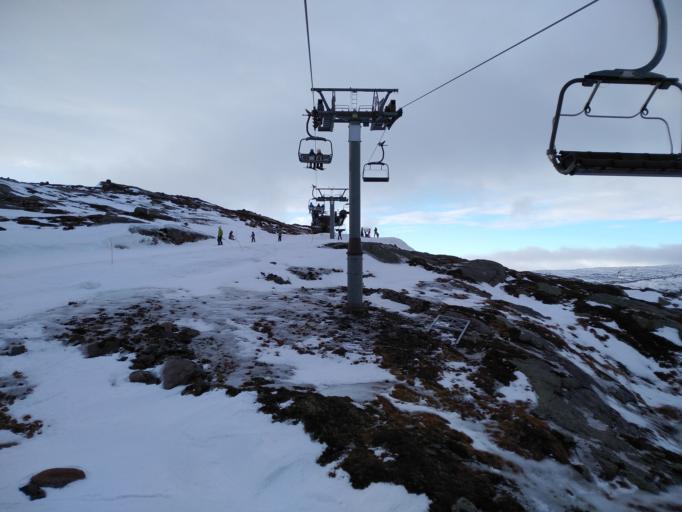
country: NO
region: Vest-Agder
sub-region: Sirdal
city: Tonstad
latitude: 58.9122
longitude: 6.8152
